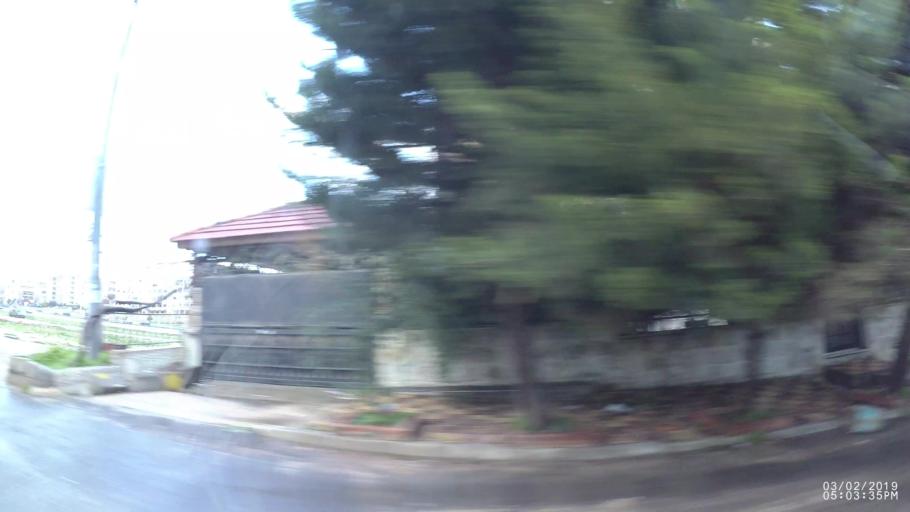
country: JO
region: Amman
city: Amman
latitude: 31.9825
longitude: 35.9168
